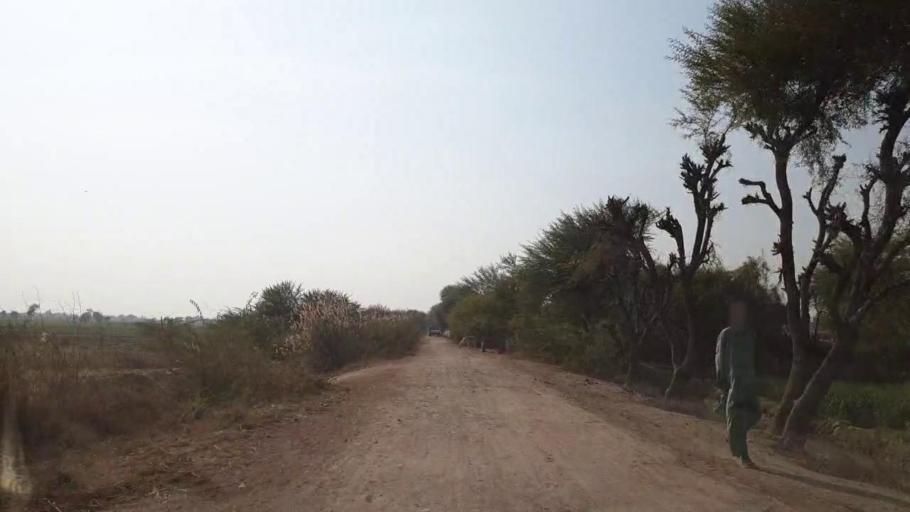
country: PK
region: Sindh
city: Pithoro
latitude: 25.6941
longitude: 69.2134
